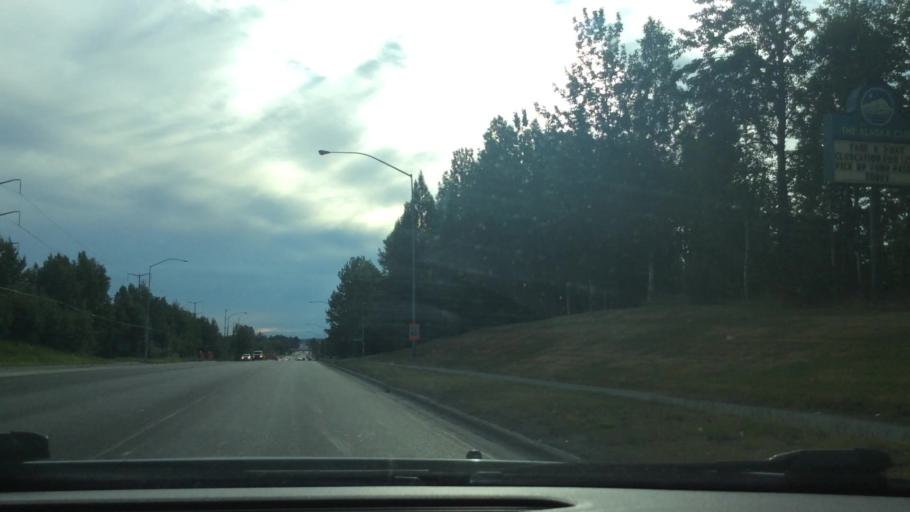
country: US
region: Alaska
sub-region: Anchorage Municipality
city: Anchorage
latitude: 61.1808
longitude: -149.7830
